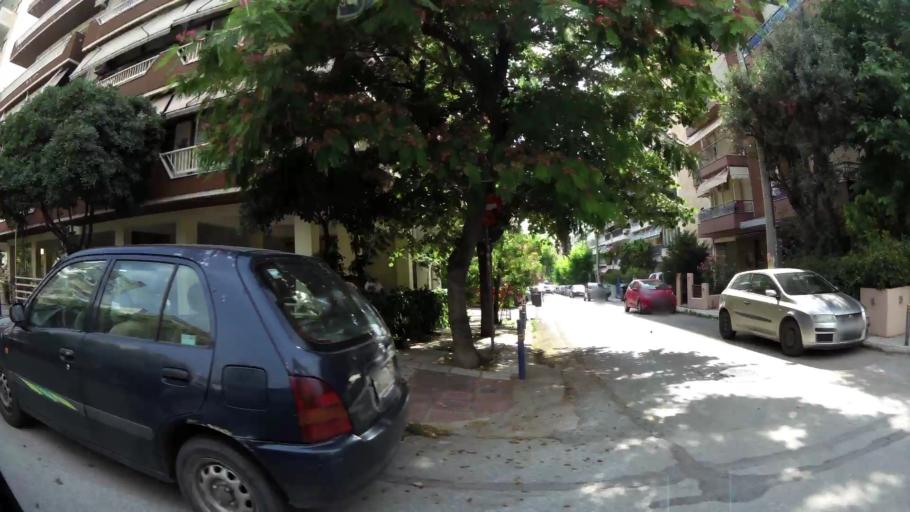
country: GR
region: Central Macedonia
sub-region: Nomos Thessalonikis
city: Kalamaria
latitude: 40.5796
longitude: 22.9579
